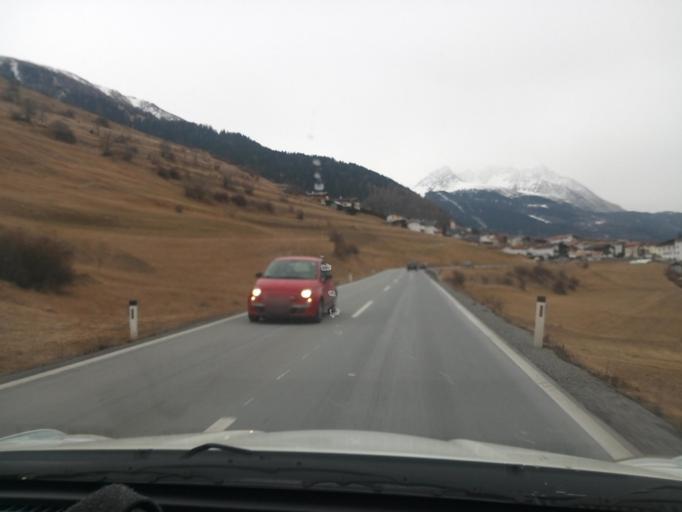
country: AT
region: Tyrol
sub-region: Politischer Bezirk Landeck
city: Nauders
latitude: 46.8992
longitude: 10.4967
